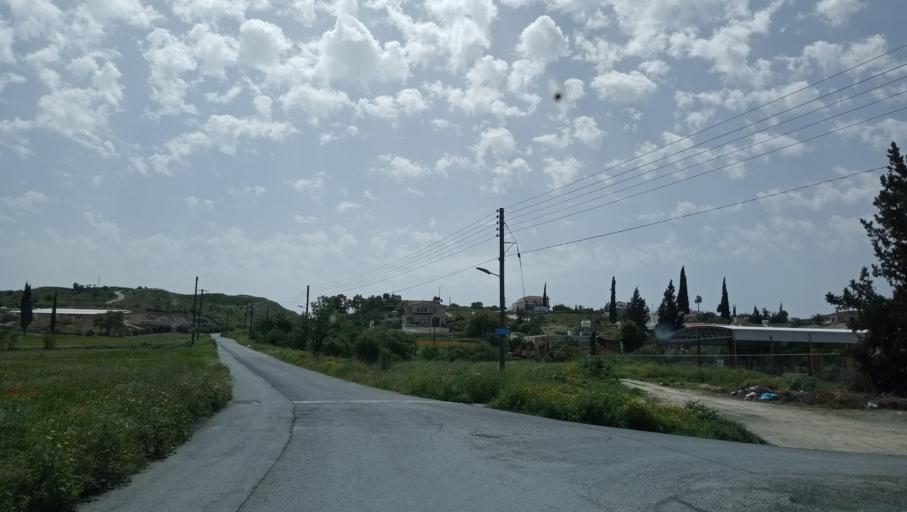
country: CY
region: Lefkosia
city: Dali
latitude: 35.0173
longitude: 33.4210
